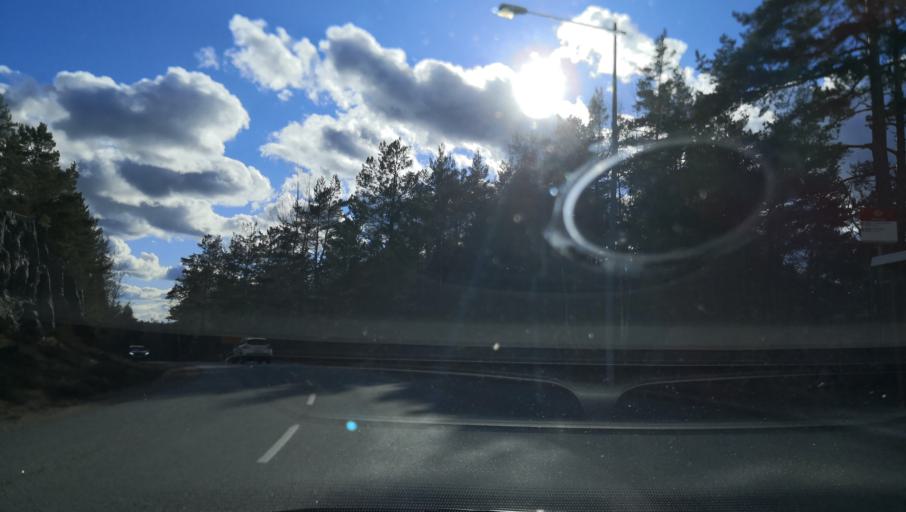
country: SE
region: Stockholm
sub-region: Varmdo Kommun
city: Mortnas
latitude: 59.2814
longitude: 18.4520
